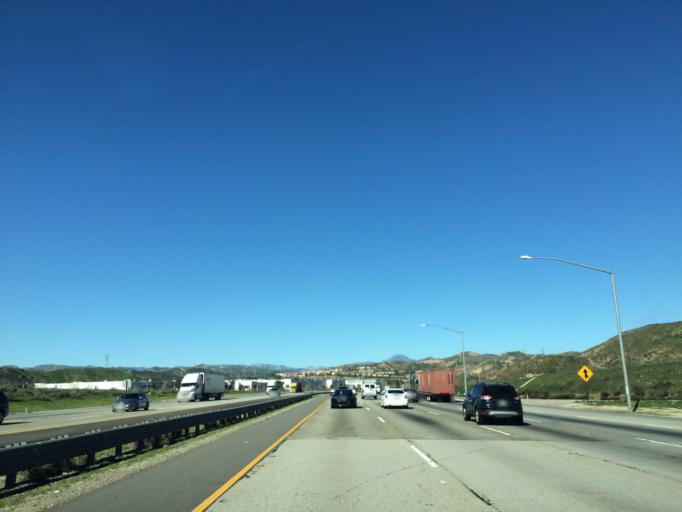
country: US
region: California
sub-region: Los Angeles County
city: Valencia
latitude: 34.4437
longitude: -118.6063
